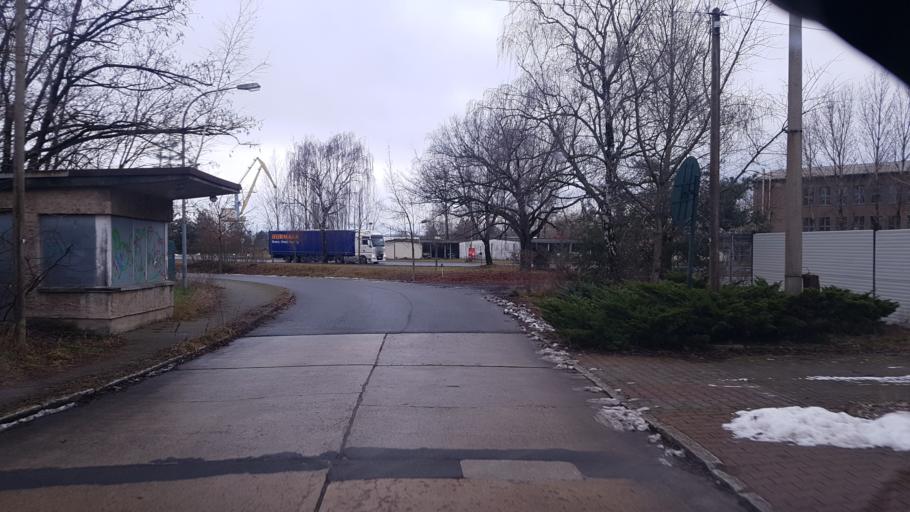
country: DE
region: Brandenburg
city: Eisenhuettenstadt
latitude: 52.1561
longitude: 14.6559
